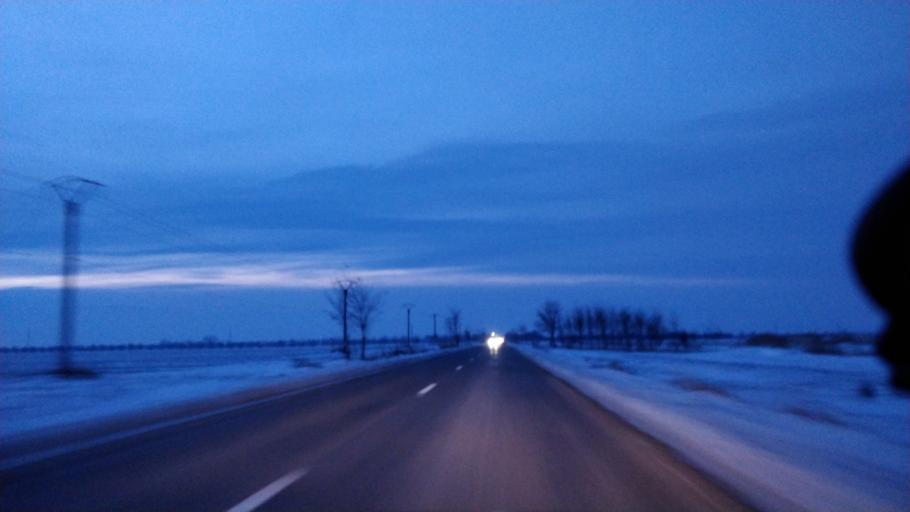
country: RO
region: Vrancea
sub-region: Comuna Vulturu
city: Vadu Rosca
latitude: 45.6041
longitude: 27.4525
